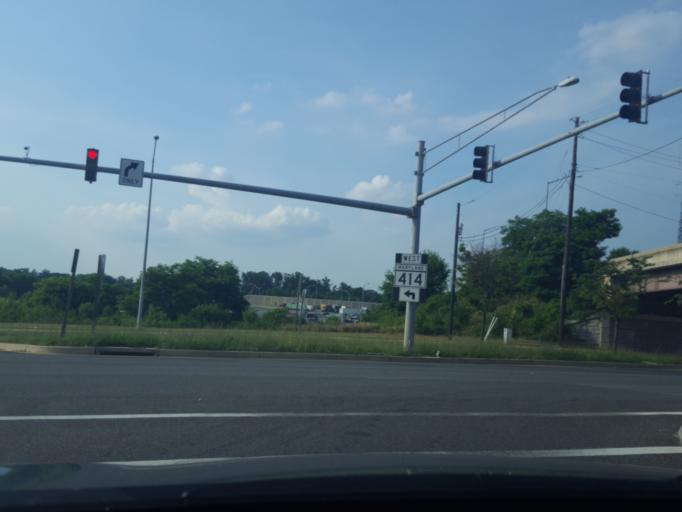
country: US
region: Maryland
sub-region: Prince George's County
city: Oxon Hill
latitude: 38.8020
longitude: -76.9971
